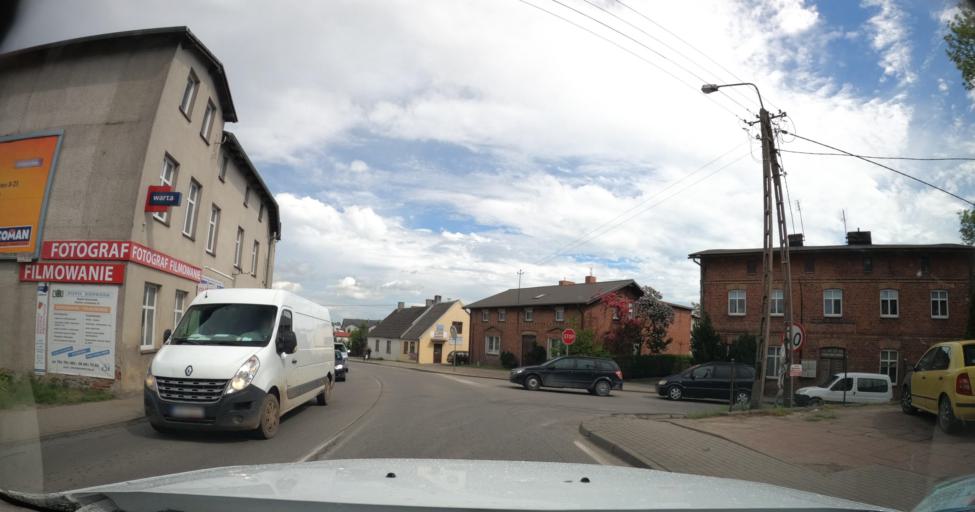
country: PL
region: Pomeranian Voivodeship
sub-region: Powiat kartuski
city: Zukowo
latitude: 54.3416
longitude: 18.3661
